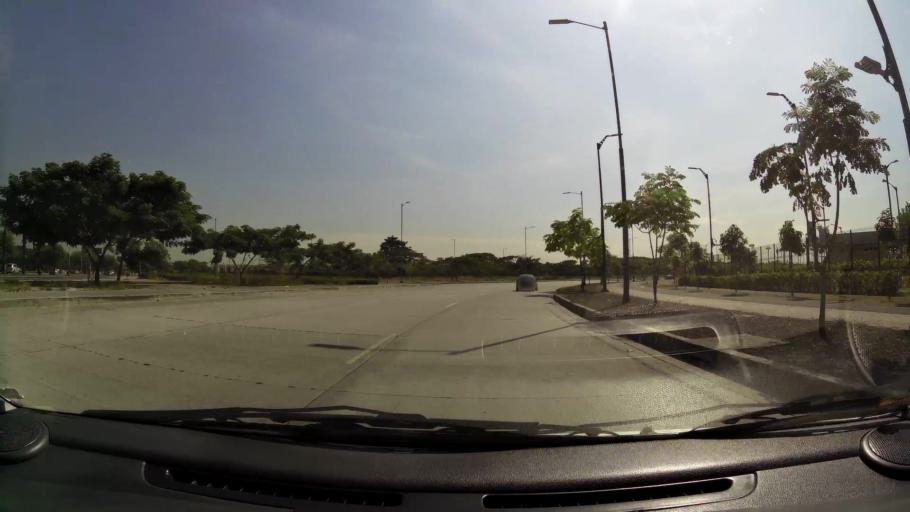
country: EC
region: Guayas
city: Eloy Alfaro
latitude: -2.1032
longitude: -79.9094
